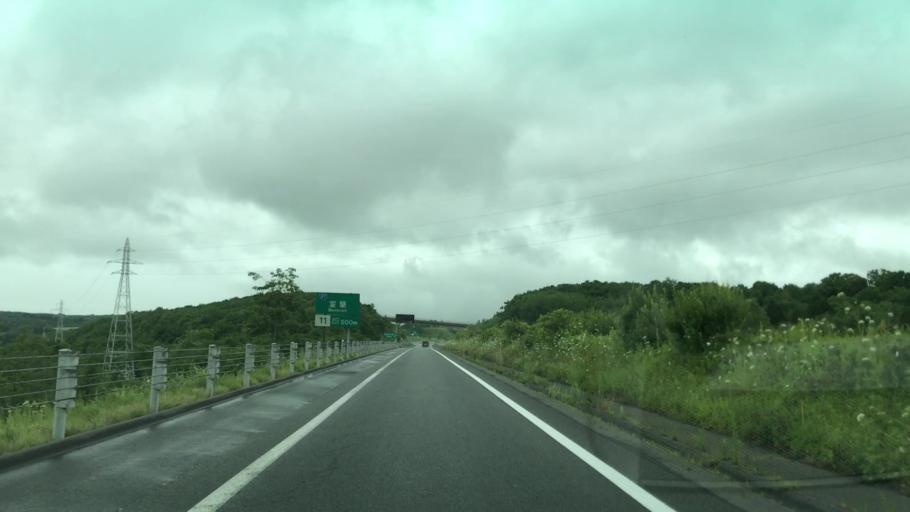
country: JP
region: Hokkaido
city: Muroran
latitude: 42.3856
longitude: 140.9811
